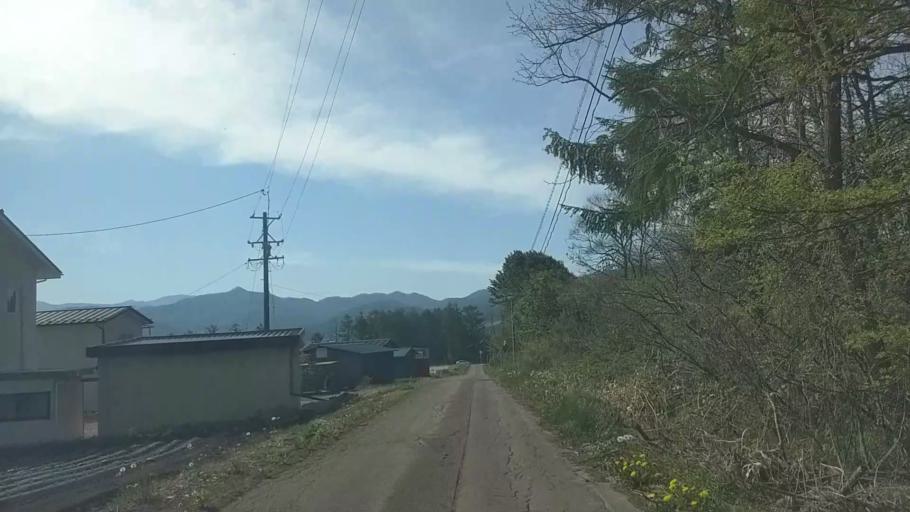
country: JP
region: Yamanashi
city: Nirasaki
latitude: 35.9494
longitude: 138.4596
